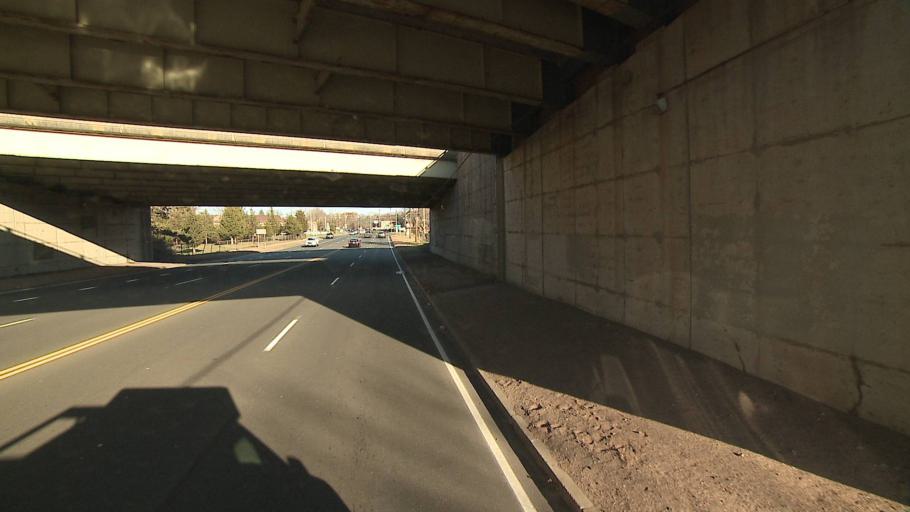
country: US
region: Connecticut
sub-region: New Haven County
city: Hamden
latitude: 41.3782
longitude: -72.8808
